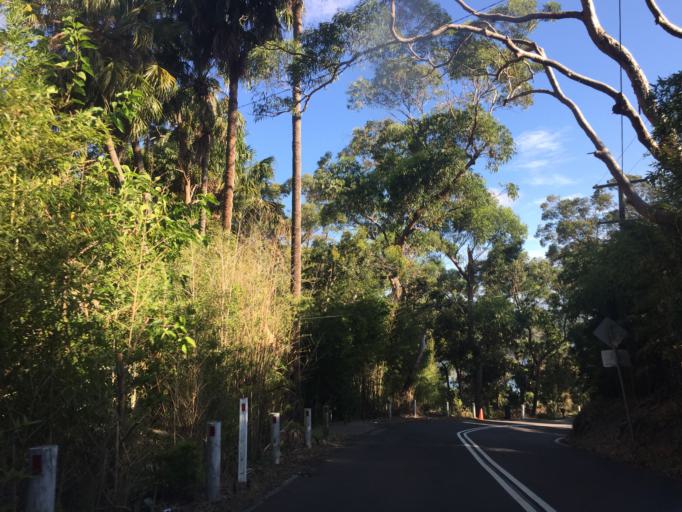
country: AU
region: New South Wales
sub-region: Pittwater
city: North Narrabeen
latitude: -33.7067
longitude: 151.2825
